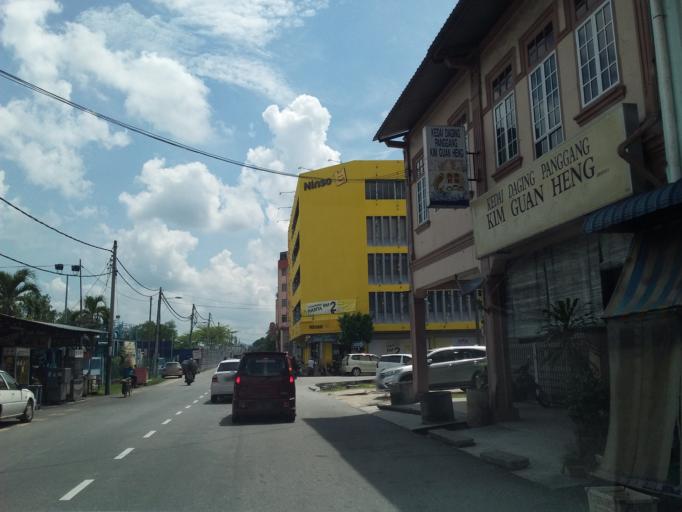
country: MY
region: Johor
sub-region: Daerah Batu Pahat
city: Batu Pahat
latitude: 1.8513
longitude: 102.9249
